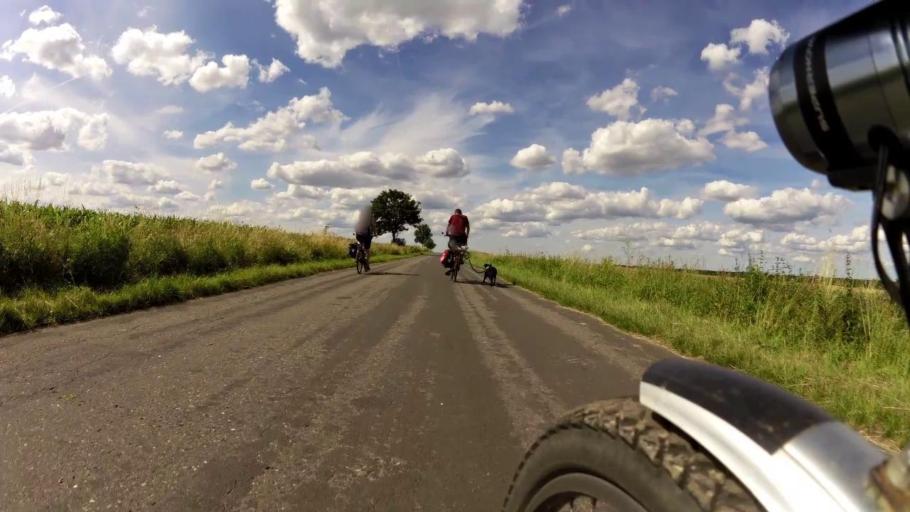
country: PL
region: West Pomeranian Voivodeship
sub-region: Powiat lobeski
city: Dobra
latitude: 53.5709
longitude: 15.4058
